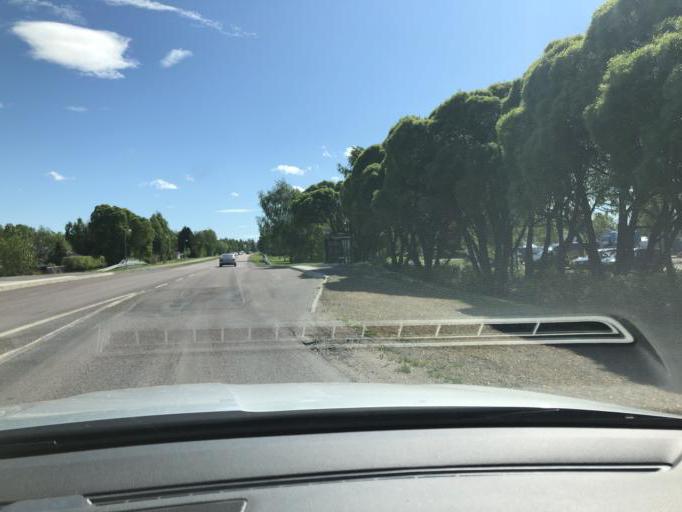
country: SE
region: Norrbotten
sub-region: Pitea Kommun
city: Pitea
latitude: 65.3238
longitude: 21.4505
